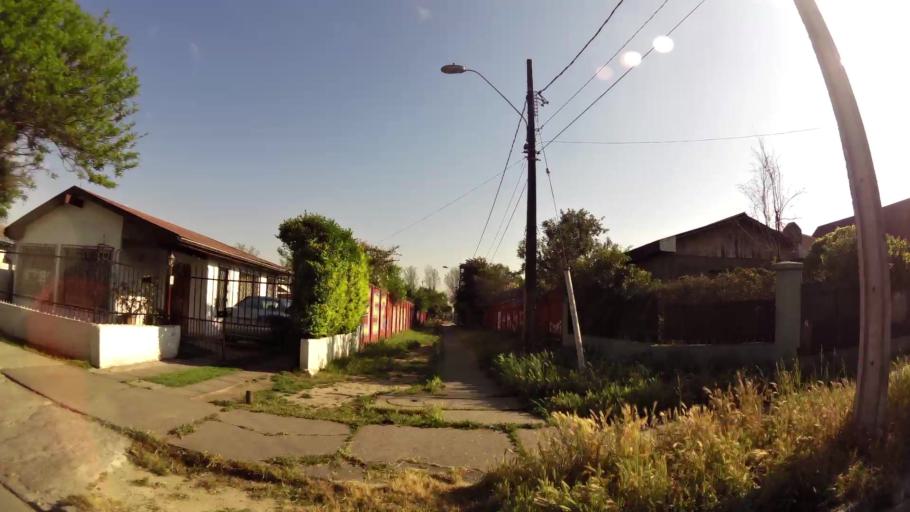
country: CL
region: Santiago Metropolitan
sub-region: Provincia de Santiago
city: La Pintana
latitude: -33.5646
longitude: -70.5891
